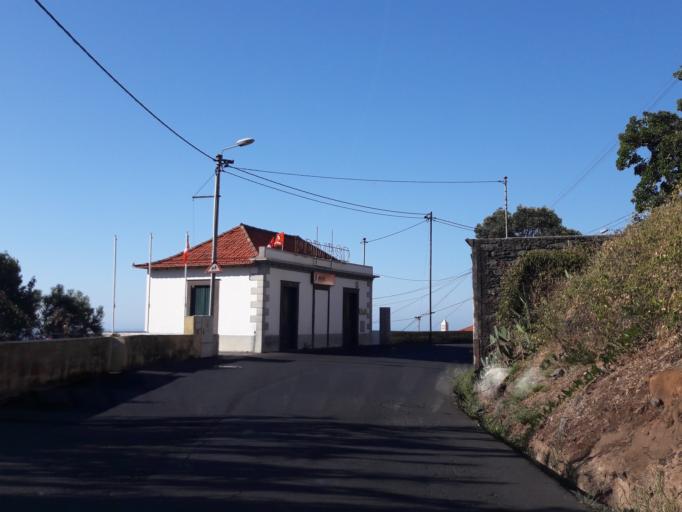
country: PT
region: Madeira
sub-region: Funchal
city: Nossa Senhora do Monte
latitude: 32.6500
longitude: -16.8811
